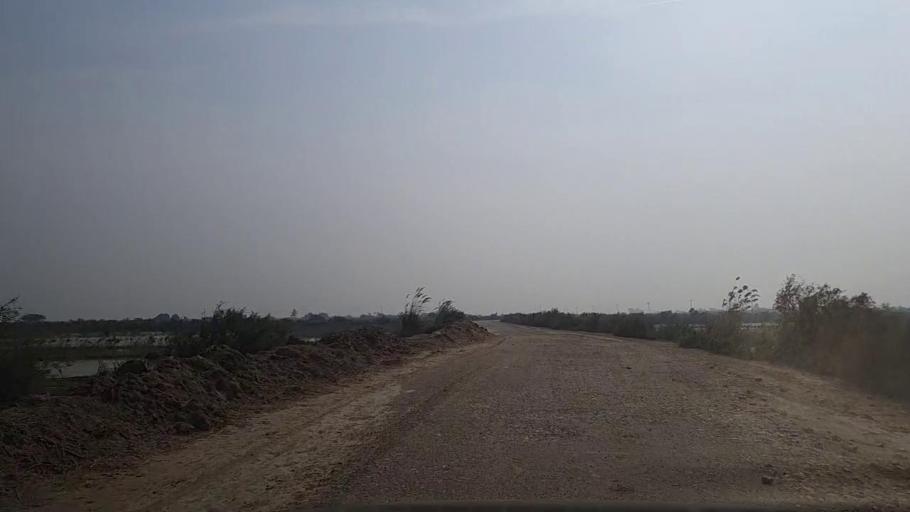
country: PK
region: Sindh
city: Mirpur Sakro
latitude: 24.4003
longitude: 67.7513
